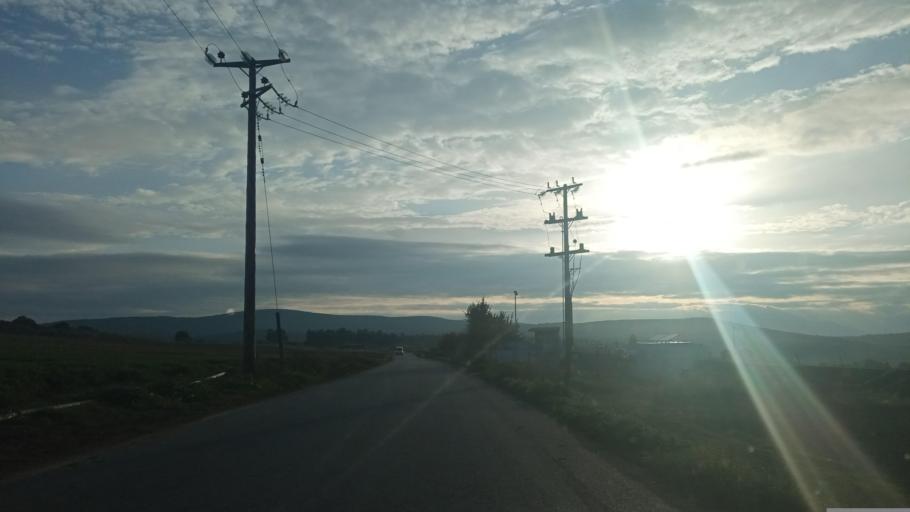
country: GR
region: Central Greece
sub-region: Nomos Evvoias
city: Kastella
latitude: 38.5749
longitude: 23.7097
